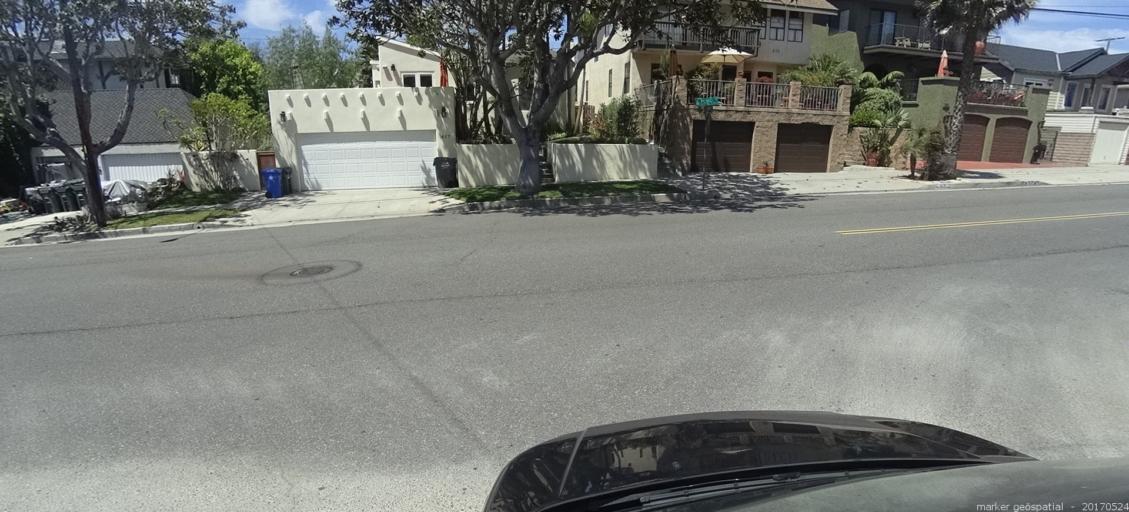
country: US
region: California
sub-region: Los Angeles County
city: Redondo Beach
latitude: 33.8360
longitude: -118.3827
